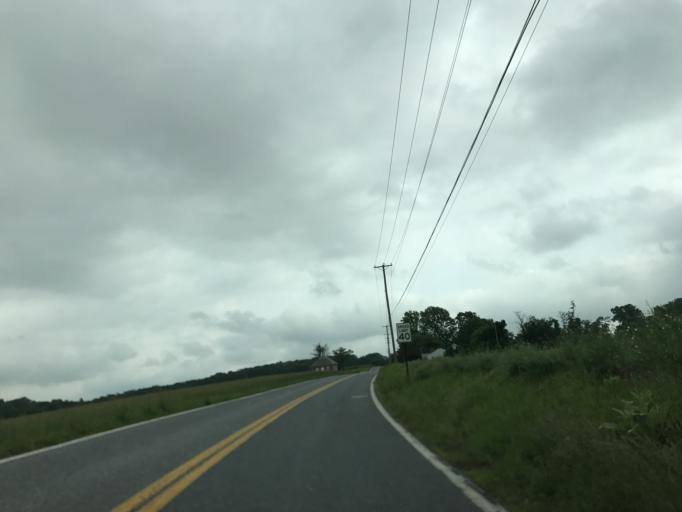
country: US
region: Pennsylvania
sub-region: York County
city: Dallastown
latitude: 39.8443
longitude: -76.6370
